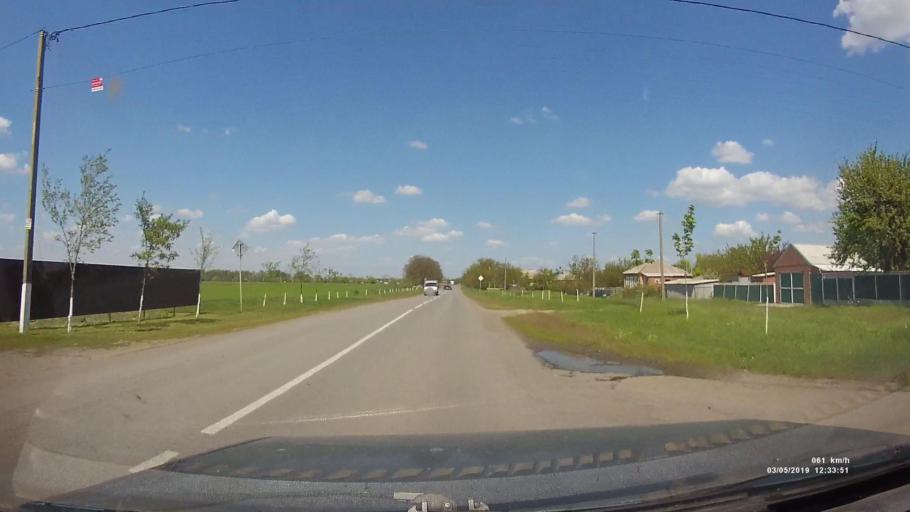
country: RU
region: Rostov
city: Semikarakorsk
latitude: 47.5164
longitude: 40.7710
